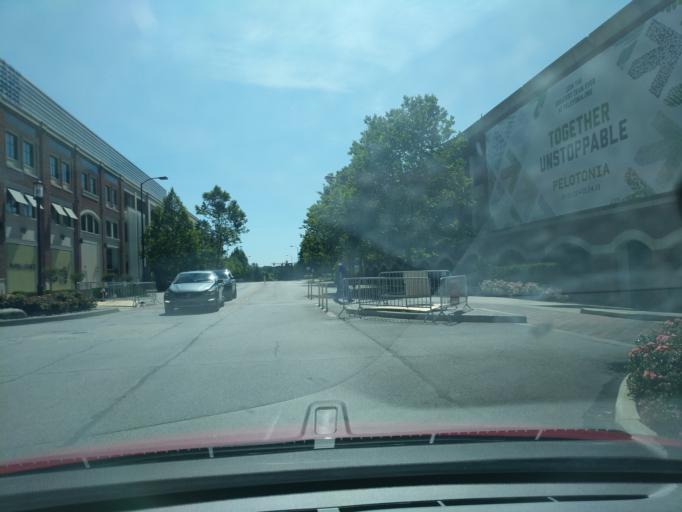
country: US
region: Ohio
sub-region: Franklin County
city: Huber Ridge
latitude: 40.0517
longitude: -82.9143
